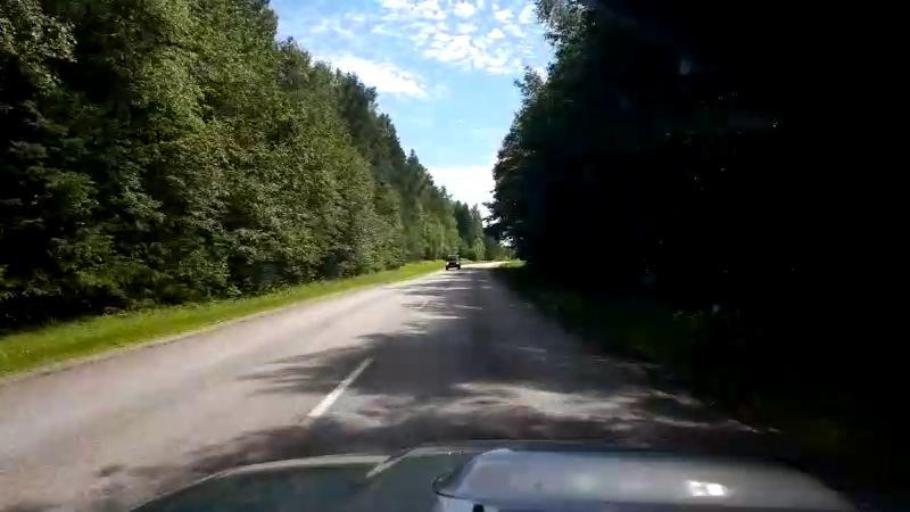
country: EE
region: Laeaene-Virumaa
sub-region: Rakke vald
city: Rakke
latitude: 58.8763
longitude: 26.2957
